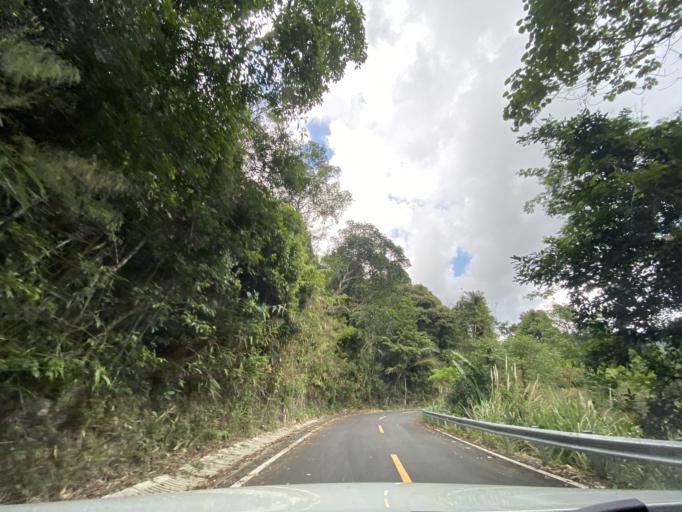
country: CN
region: Hainan
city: Benhao
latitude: 18.6834
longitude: 109.8795
